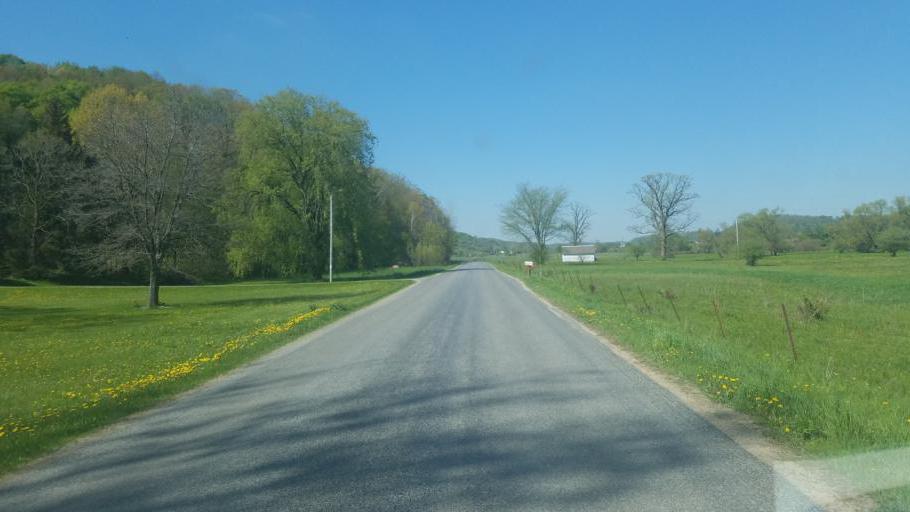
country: US
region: Wisconsin
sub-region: Vernon County
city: Hillsboro
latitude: 43.6258
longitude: -90.3633
